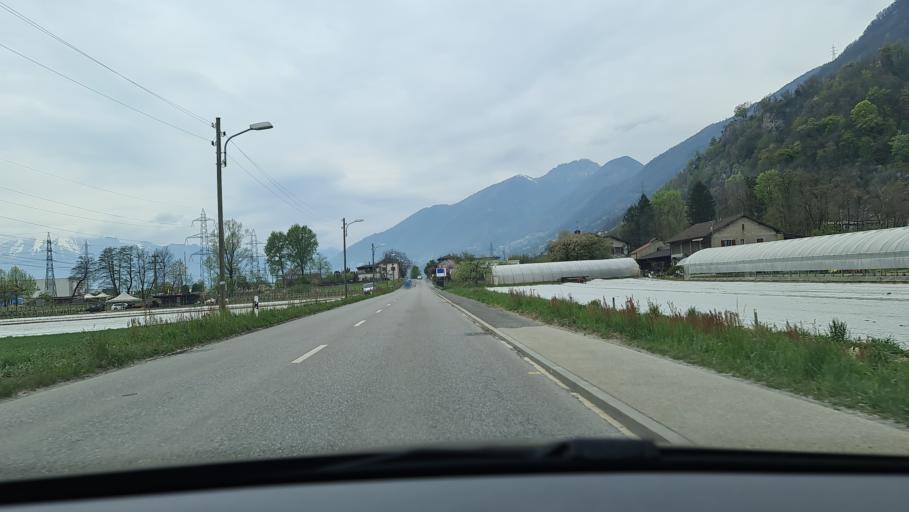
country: CH
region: Ticino
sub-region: Locarno District
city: Cugnasco
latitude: 46.1739
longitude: 8.9031
